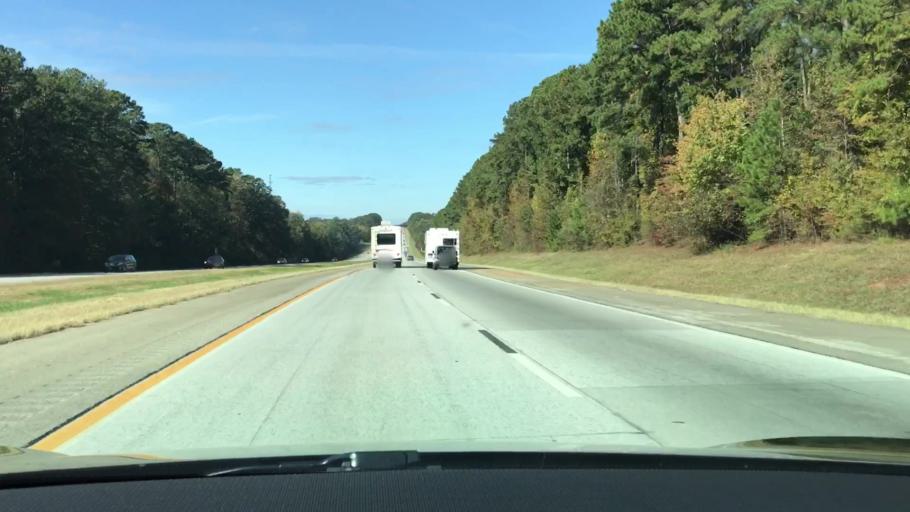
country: US
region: Georgia
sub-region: Putnam County
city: Jefferson
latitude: 33.5335
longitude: -83.2940
